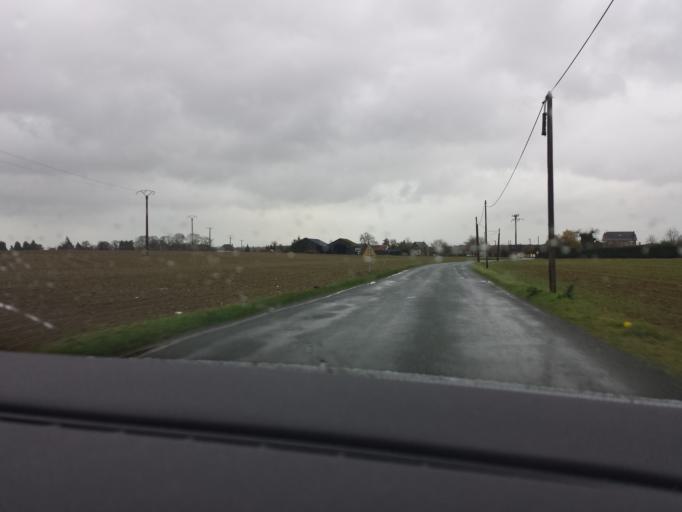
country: FR
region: Haute-Normandie
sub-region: Departement de l'Eure
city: Evreux
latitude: 49.0111
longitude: 1.1929
